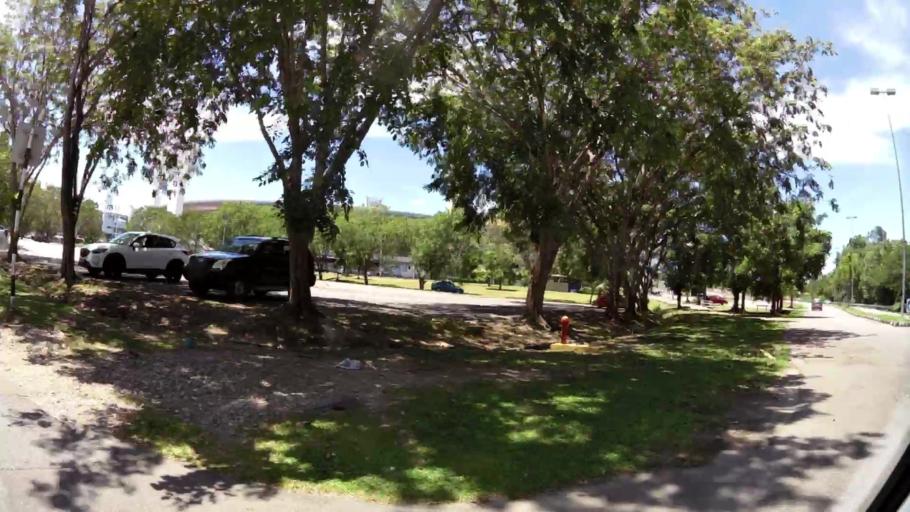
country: BN
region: Brunei and Muara
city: Bandar Seri Begawan
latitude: 4.9310
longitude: 114.9444
